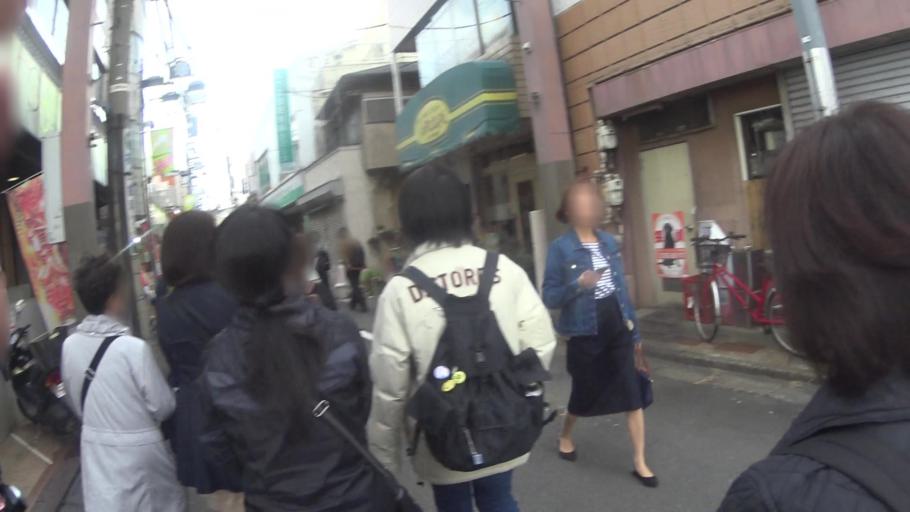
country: JP
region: Tokyo
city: Tokyo
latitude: 35.6832
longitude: 139.6842
